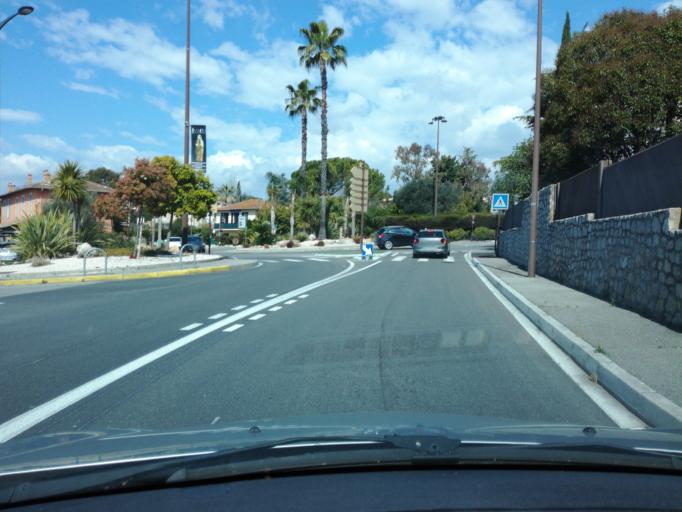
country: FR
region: Provence-Alpes-Cote d'Azur
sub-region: Departement des Alpes-Maritimes
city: Mougins
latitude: 43.6045
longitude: 7.0088
